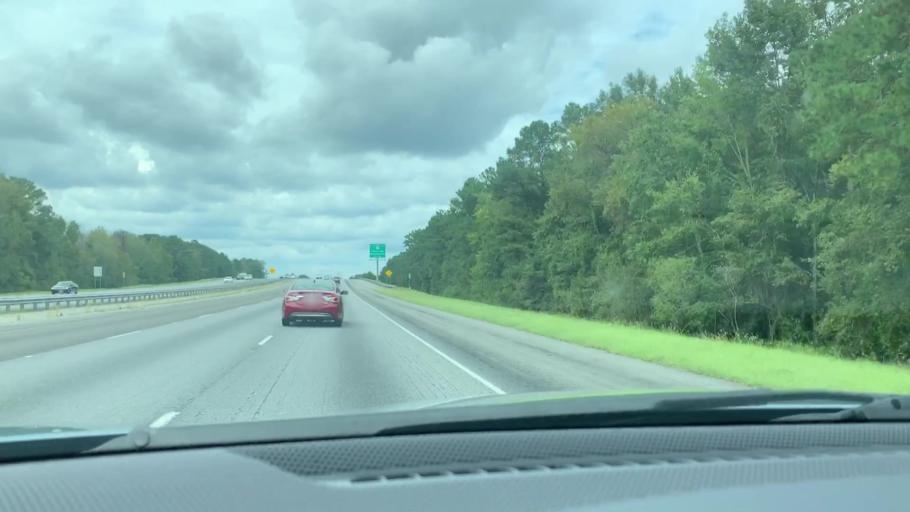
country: US
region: Georgia
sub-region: Bryan County
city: Richmond Hill
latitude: 31.9072
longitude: -81.3379
